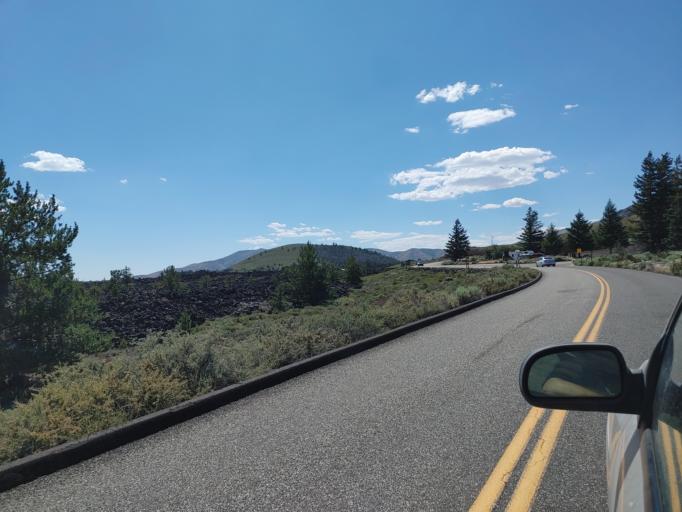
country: US
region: Idaho
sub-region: Butte County
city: Arco
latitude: 43.4619
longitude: -113.5592
